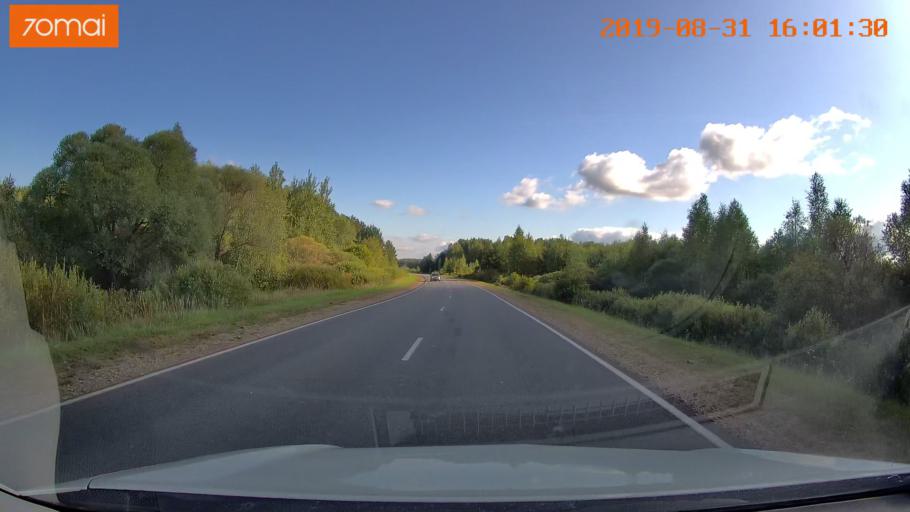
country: RU
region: Kaluga
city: Yukhnov
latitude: 54.6886
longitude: 35.2904
